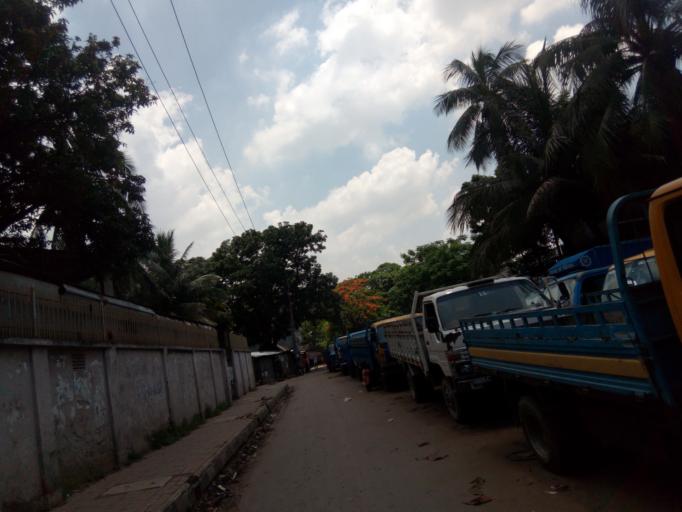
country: BD
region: Dhaka
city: Paltan
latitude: 23.7560
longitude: 90.3981
